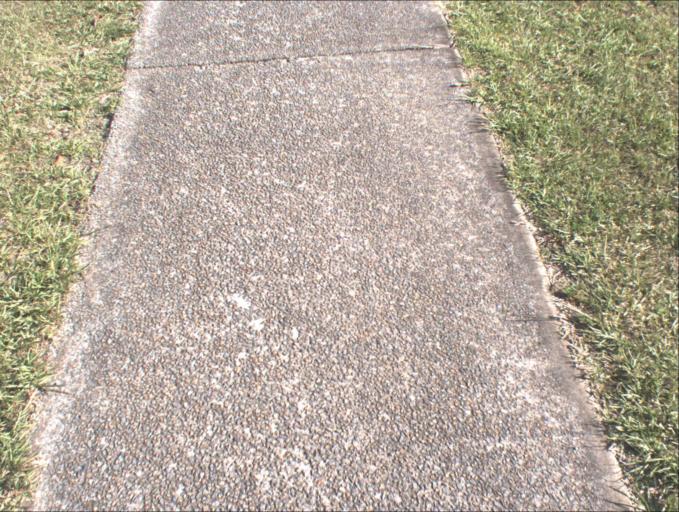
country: AU
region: Queensland
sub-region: Logan
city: Logan City
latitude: -27.6559
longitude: 153.0980
